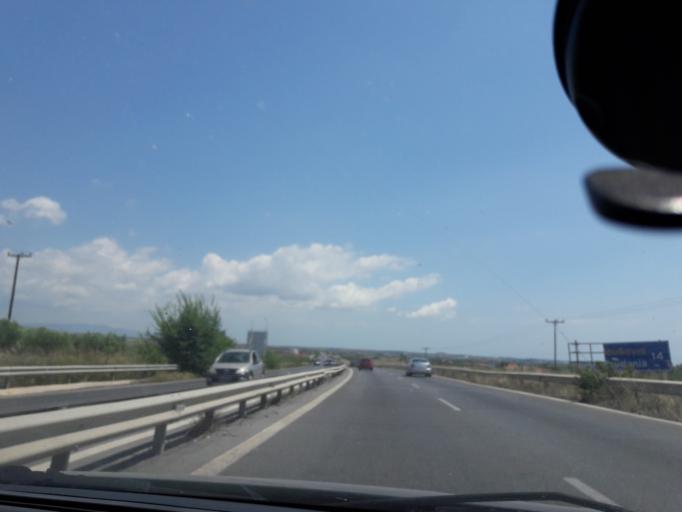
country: GR
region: Central Macedonia
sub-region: Nomos Chalkidikis
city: Nea Plagia
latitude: 40.2842
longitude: 23.1558
